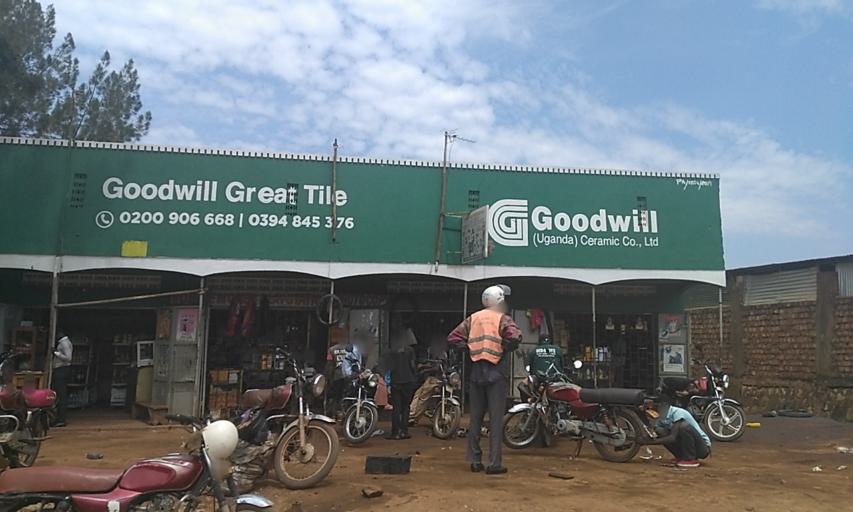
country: UG
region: Central Region
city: Kampala Central Division
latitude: 0.3033
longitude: 32.5431
